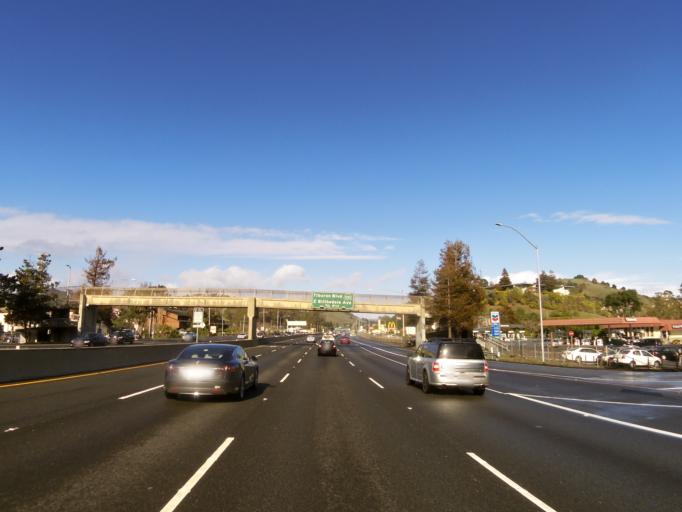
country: US
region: California
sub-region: Marin County
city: Strawberry
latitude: 37.8885
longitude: -122.5167
